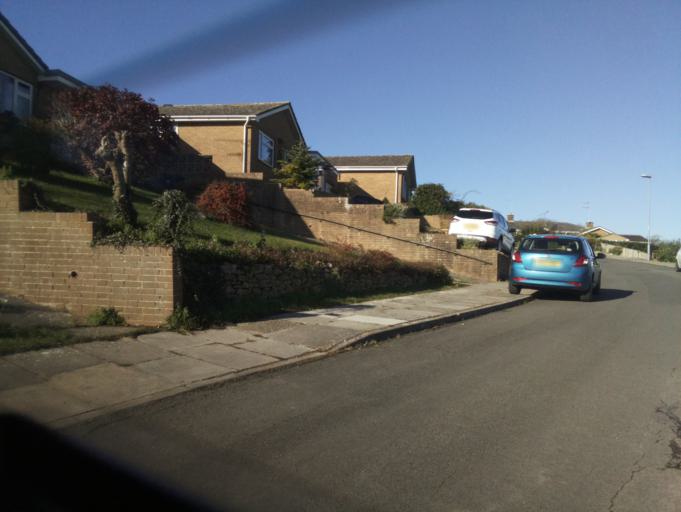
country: GB
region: England
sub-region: Dorset
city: Sherborne
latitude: 50.9535
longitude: -2.5049
